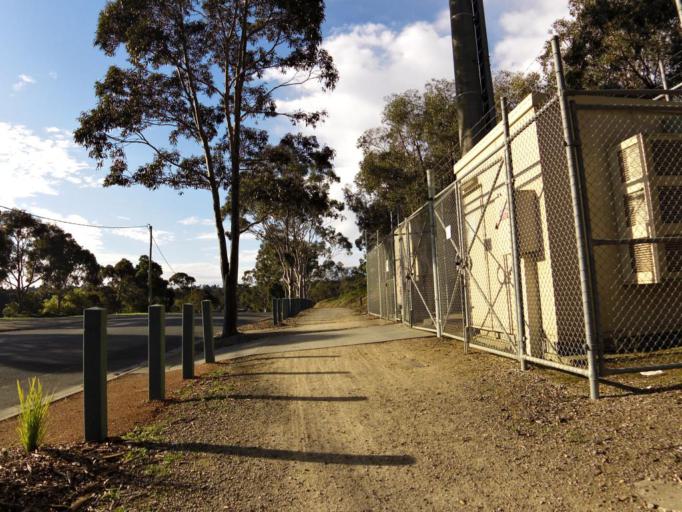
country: AU
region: Victoria
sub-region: Whitehorse
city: Vermont South
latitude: -37.8608
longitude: 145.1979
